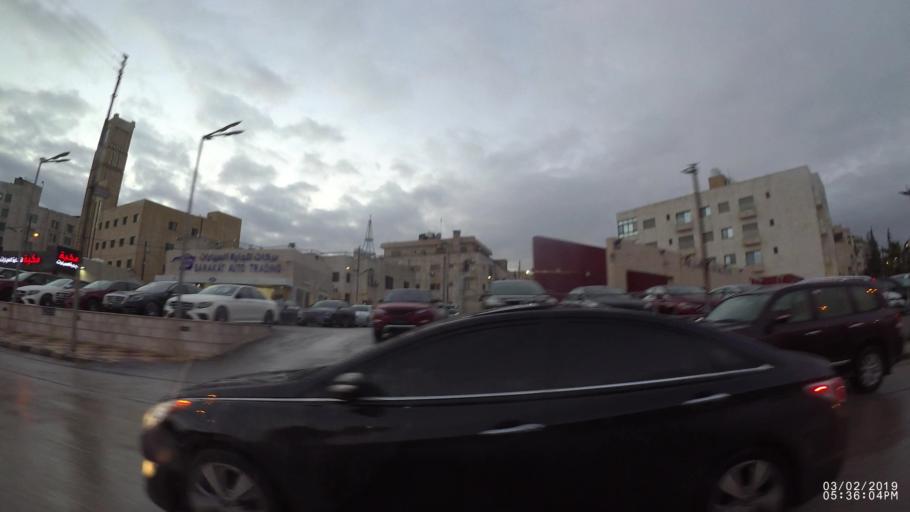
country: JO
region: Amman
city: Al Jubayhah
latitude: 31.9771
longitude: 35.8882
